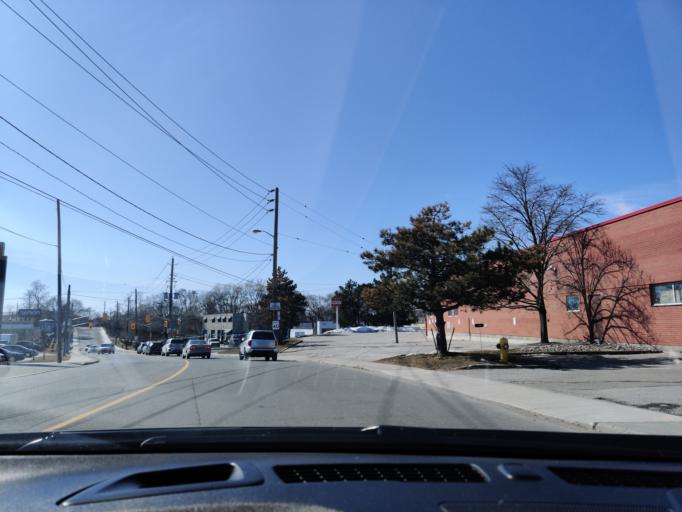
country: CA
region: Ontario
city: Toronto
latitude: 43.6977
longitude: -79.4670
